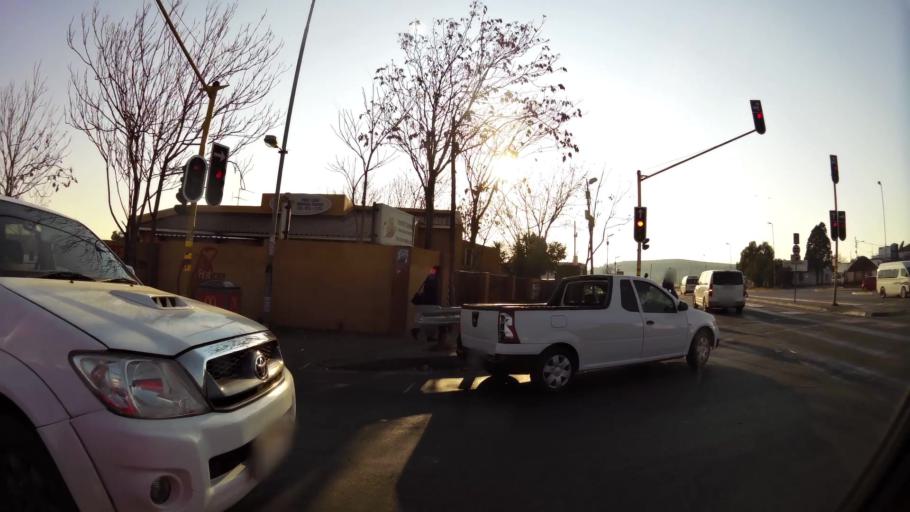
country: ZA
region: Gauteng
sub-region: City of Johannesburg Metropolitan Municipality
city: Soweto
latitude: -26.2272
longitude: 27.9321
